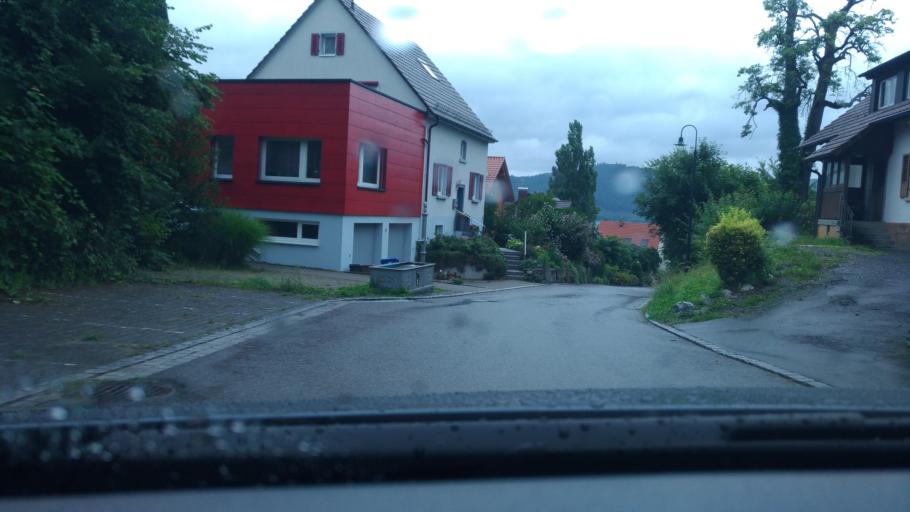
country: DE
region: Baden-Wuerttemberg
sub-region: Freiburg Region
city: Bodman-Ludwigshafen
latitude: 47.7952
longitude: 9.0465
